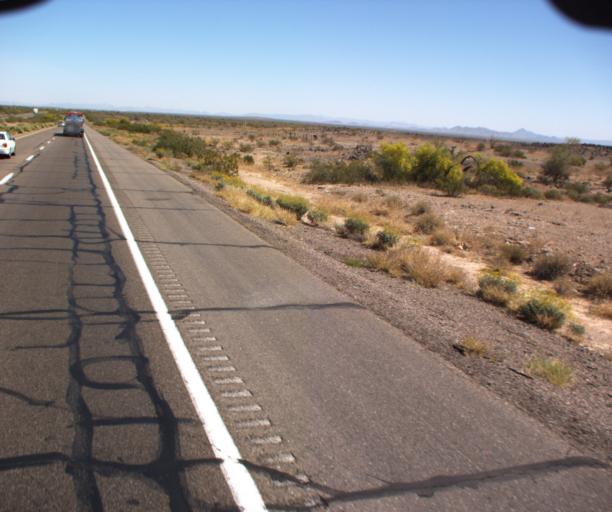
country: US
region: Arizona
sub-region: Maricopa County
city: Gila Bend
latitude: 32.8908
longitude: -113.0578
